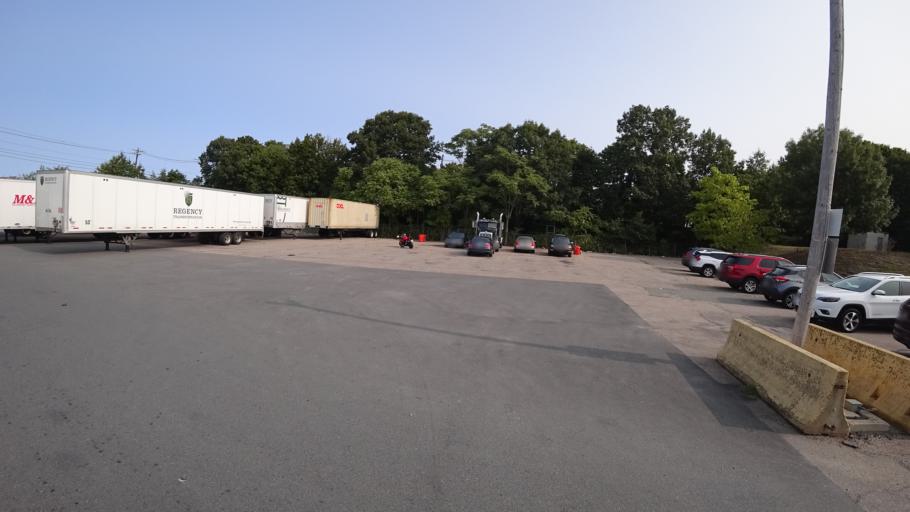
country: US
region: Massachusetts
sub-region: Norfolk County
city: Dedham
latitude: 42.2325
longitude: -71.1345
